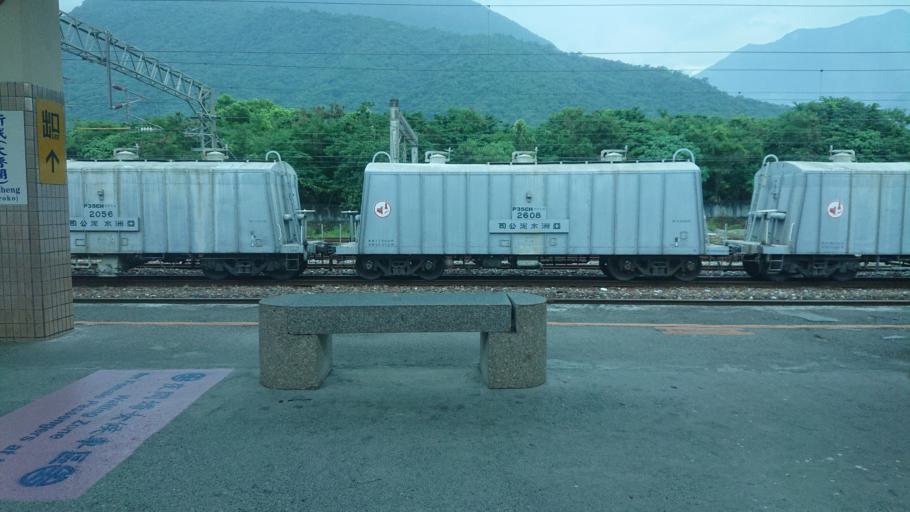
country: TW
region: Taiwan
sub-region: Hualien
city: Hualian
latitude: 24.1280
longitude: 121.6404
